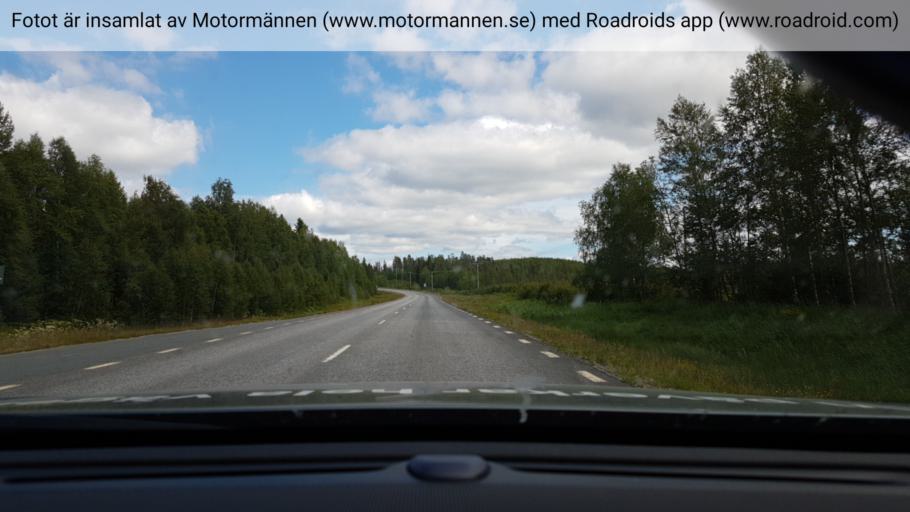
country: SE
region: Vaesterbotten
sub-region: Sorsele Kommun
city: Sorsele
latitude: 65.5363
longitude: 17.6015
